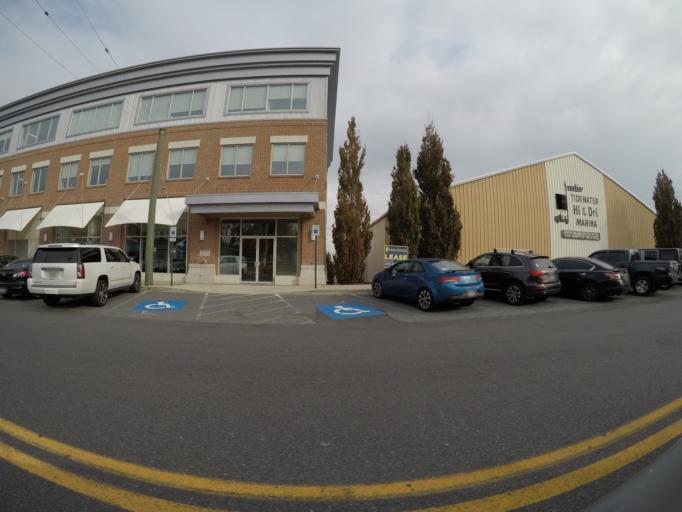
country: US
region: Maryland
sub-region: Harford County
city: Havre de Grace
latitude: 39.5460
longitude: -76.0880
